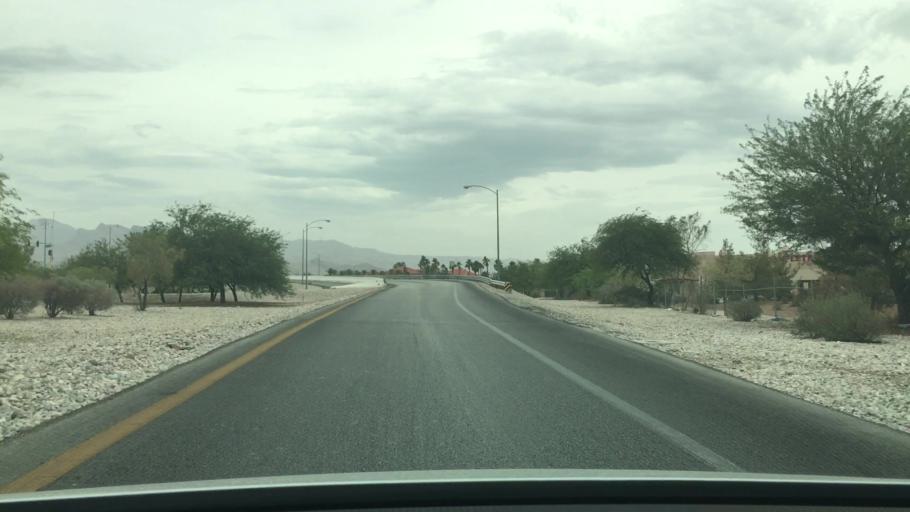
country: US
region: Nevada
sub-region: Clark County
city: Spring Valley
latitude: 36.1791
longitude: -115.2575
